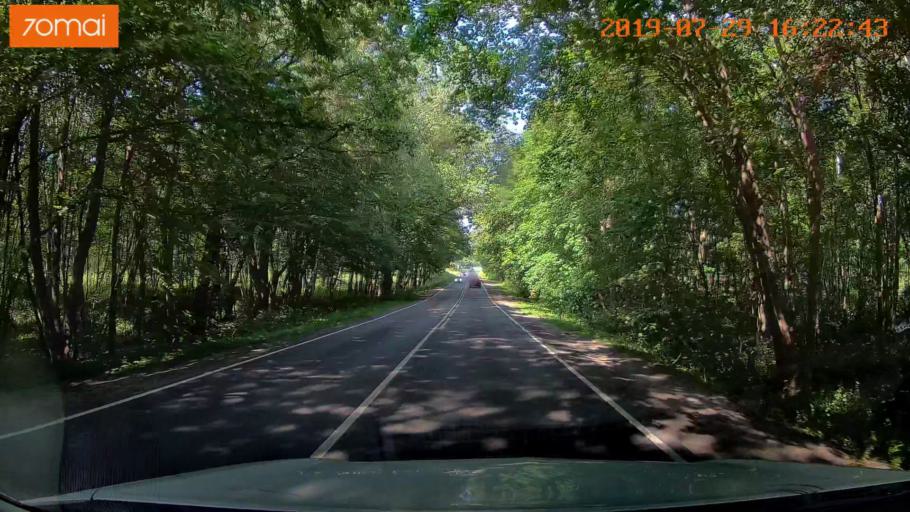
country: RU
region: Kaliningrad
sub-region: Gorod Kaliningrad
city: Baltiysk
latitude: 54.7003
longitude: 19.9408
